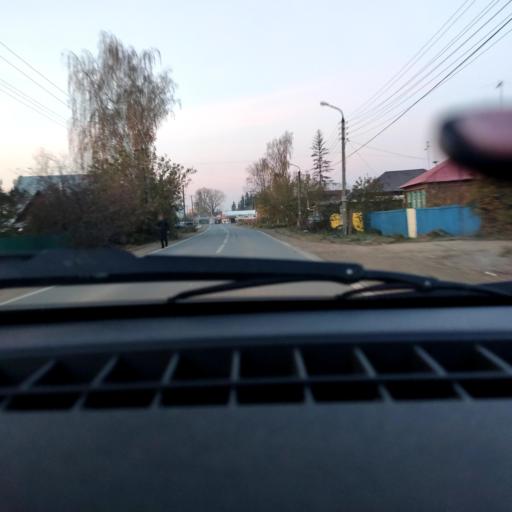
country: RU
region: Bashkortostan
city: Iglino
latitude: 54.8287
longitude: 56.1870
